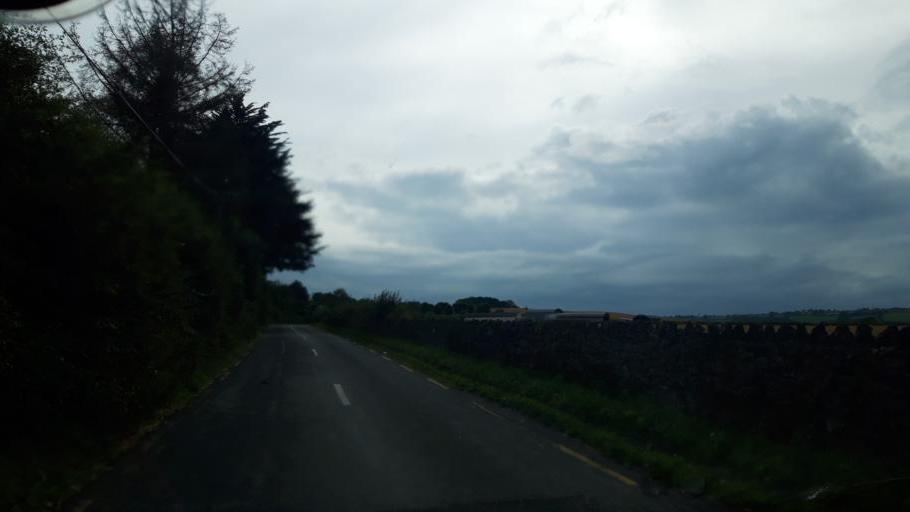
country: IE
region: Leinster
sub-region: Kilkenny
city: Ballyragget
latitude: 52.7650
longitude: -7.3588
